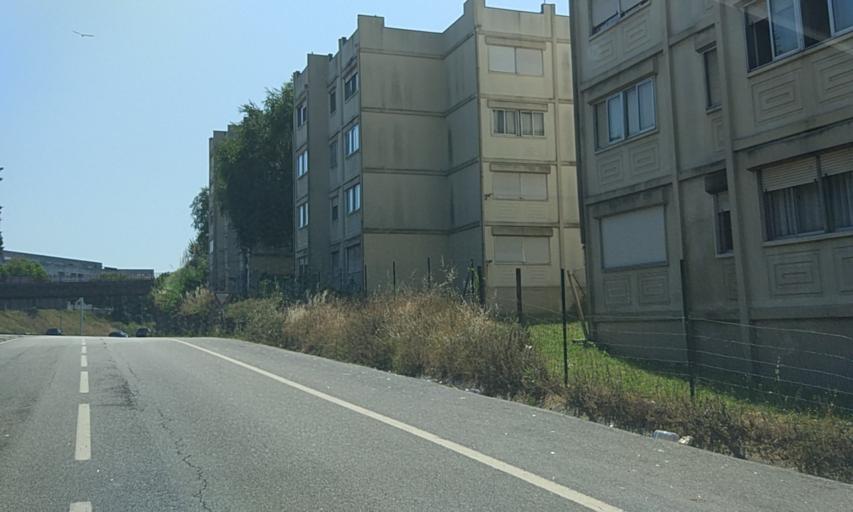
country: PT
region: Porto
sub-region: Porto
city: Porto
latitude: 41.1731
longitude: -8.6097
